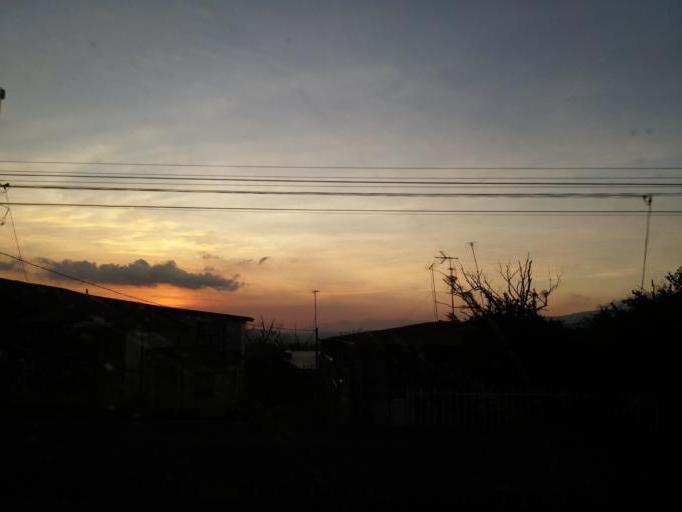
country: CR
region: Alajuela
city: Sabanilla
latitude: 10.0748
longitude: -84.2168
